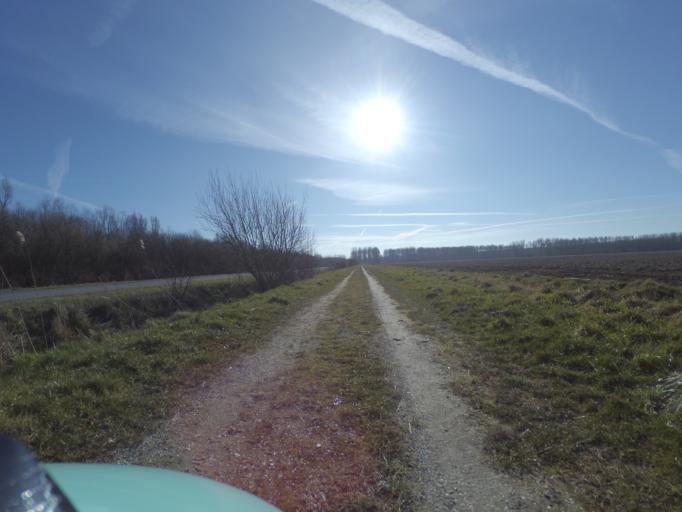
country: NL
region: Flevoland
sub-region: Gemeente Almere
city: Almere Stad
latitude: 52.3895
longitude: 5.1657
